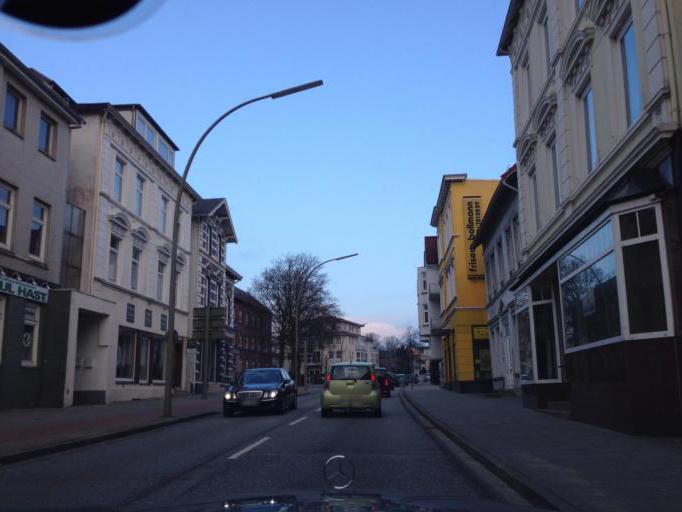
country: DE
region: Hamburg
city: Bergedorf
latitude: 53.4867
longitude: 10.2170
